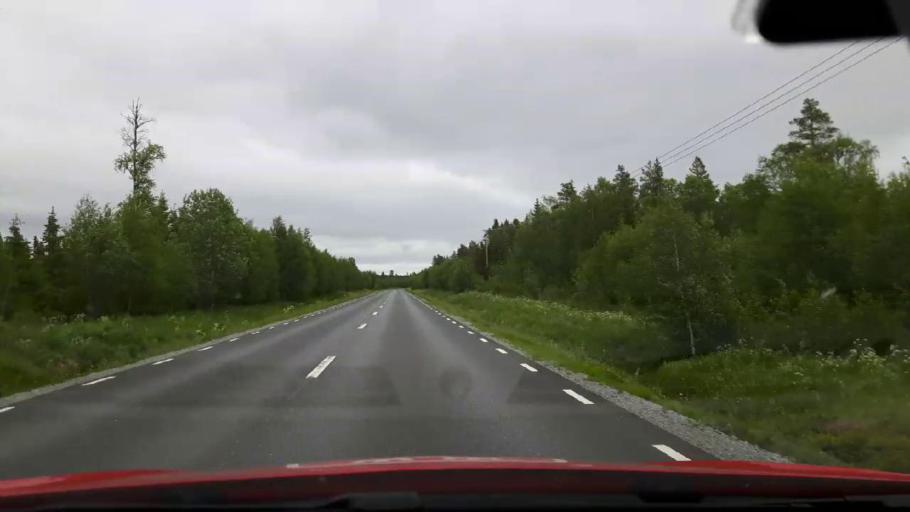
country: SE
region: Jaemtland
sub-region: OEstersunds Kommun
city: Lit
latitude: 63.7372
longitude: 14.7539
